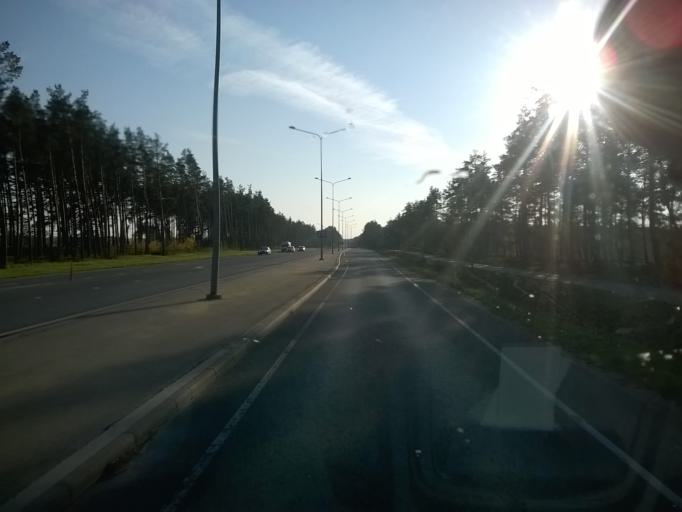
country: EE
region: Harju
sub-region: Saku vald
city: Saku
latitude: 59.3347
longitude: 24.6976
